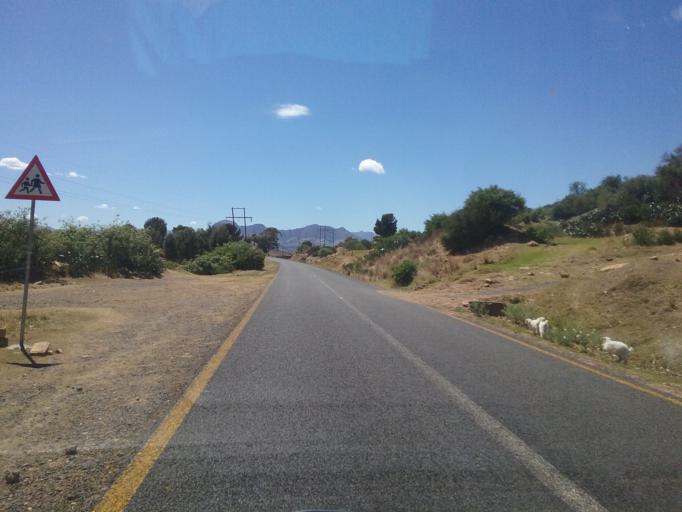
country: LS
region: Quthing
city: Quthing
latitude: -30.2777
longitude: 27.7424
